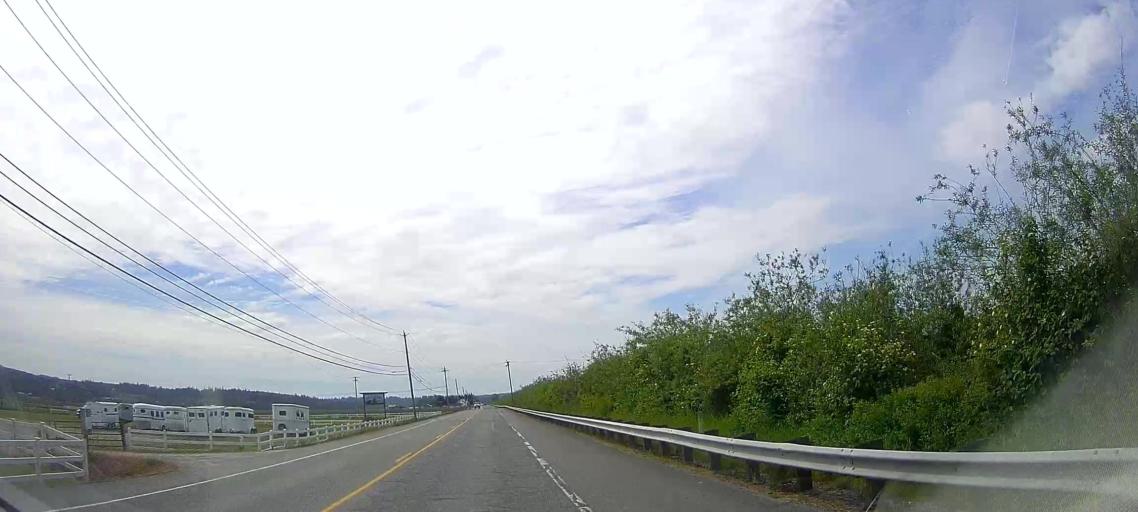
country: US
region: Washington
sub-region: Skagit County
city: Mount Vernon
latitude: 48.3571
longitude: -122.3348
